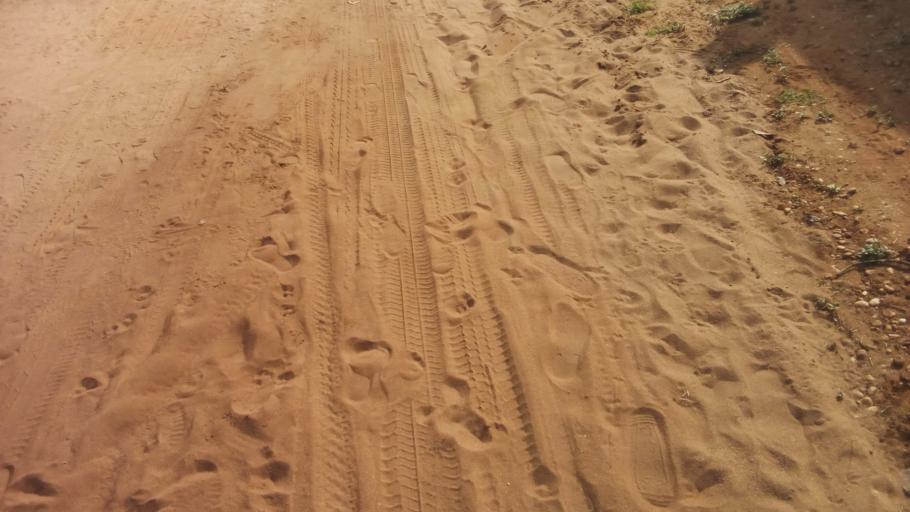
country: BJ
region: Atlantique
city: Abomey-Calavi
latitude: 6.4273
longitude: 2.3301
